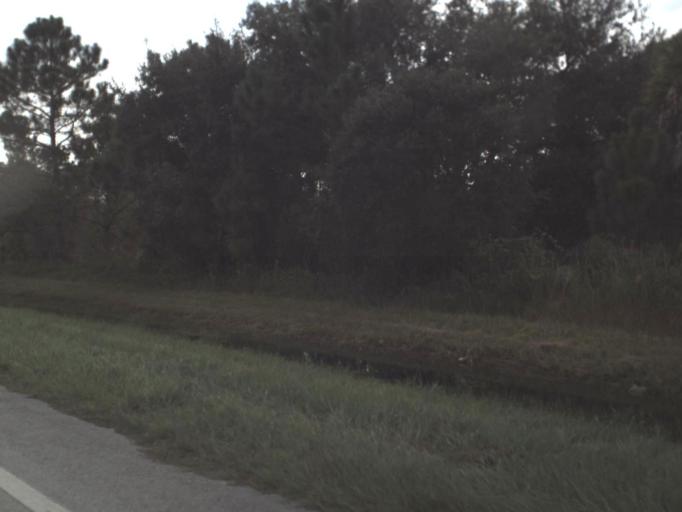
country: US
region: Florida
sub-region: Okeechobee County
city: Cypress Quarters
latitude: 27.3399
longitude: -80.8227
